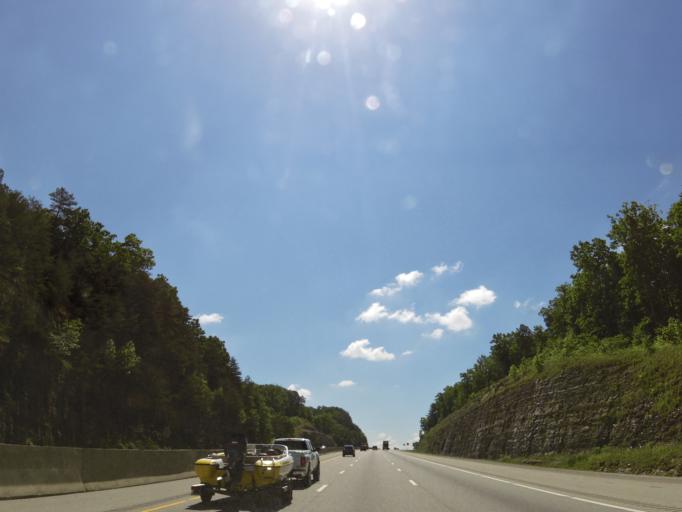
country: US
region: Kentucky
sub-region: Rockcastle County
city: Mount Vernon
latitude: 37.2309
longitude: -84.2239
